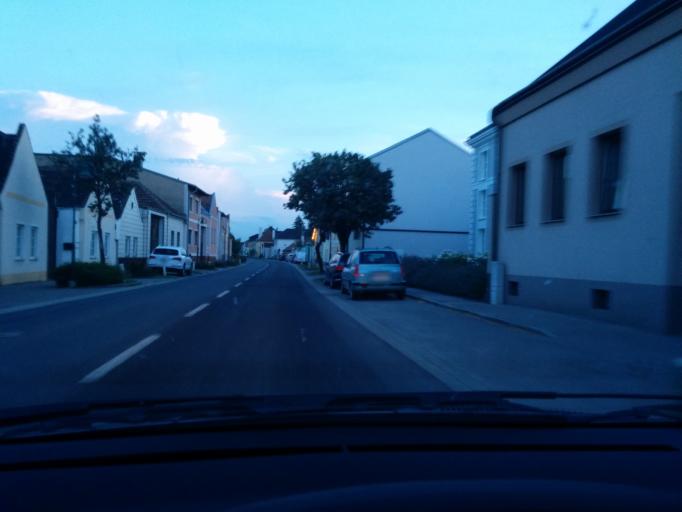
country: AT
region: Lower Austria
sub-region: Politischer Bezirk Modling
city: Munchendorf
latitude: 48.0322
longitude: 16.3812
